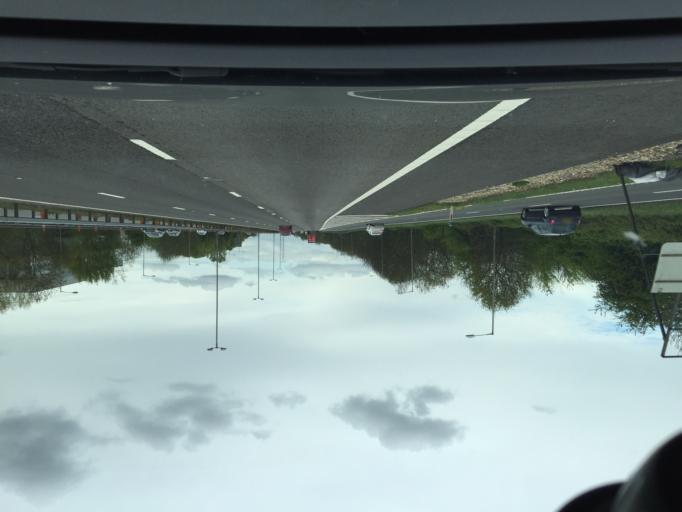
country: GB
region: England
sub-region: West Berkshire
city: Calcot
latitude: 51.4376
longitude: -1.0621
